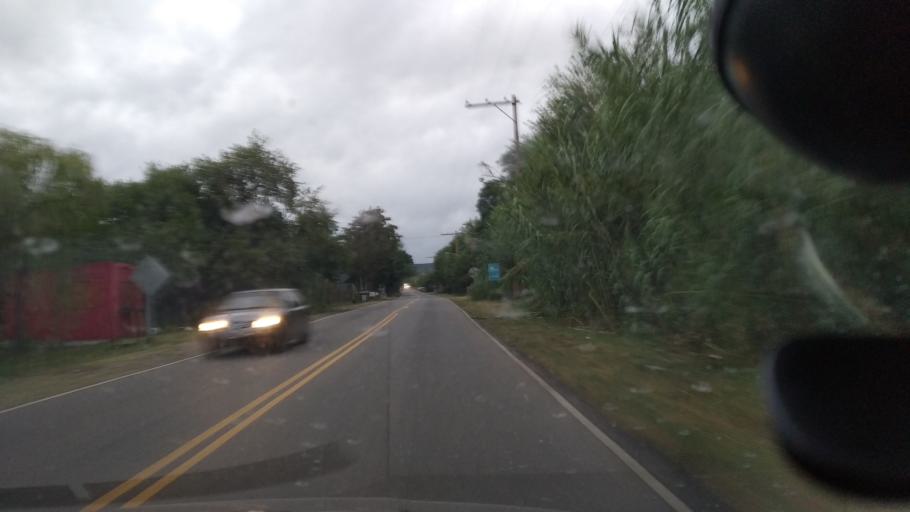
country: AR
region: Cordoba
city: Villa Las Rosas
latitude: -31.9358
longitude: -65.0411
